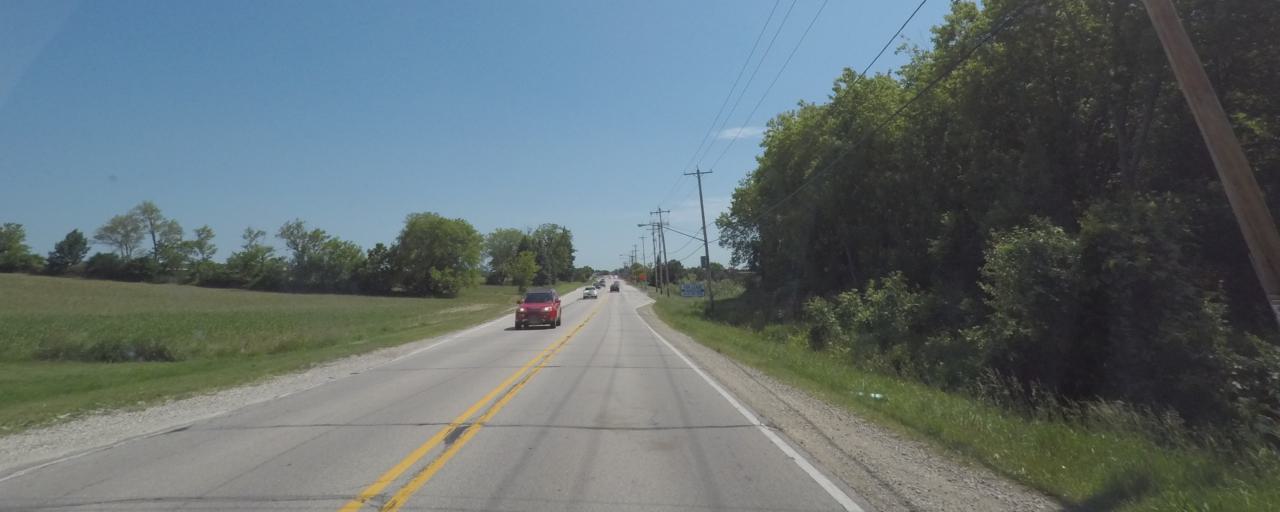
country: US
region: Wisconsin
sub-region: Milwaukee County
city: Oak Creek
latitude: 42.8791
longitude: -87.9321
